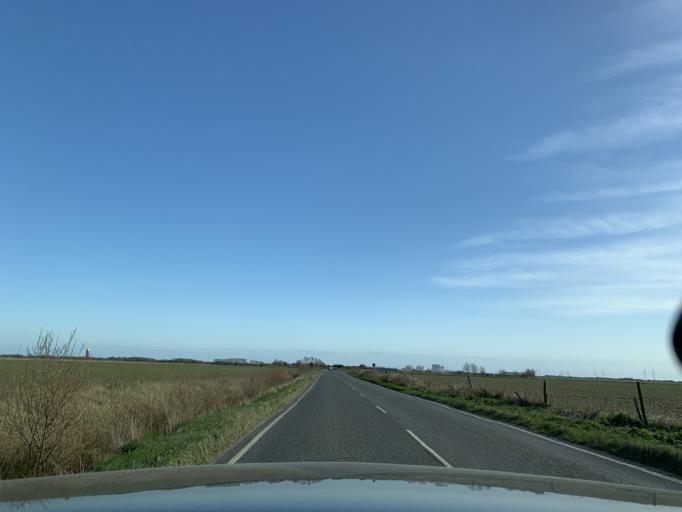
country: GB
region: England
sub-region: Kent
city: Lydd
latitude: 50.9486
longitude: 0.9178
